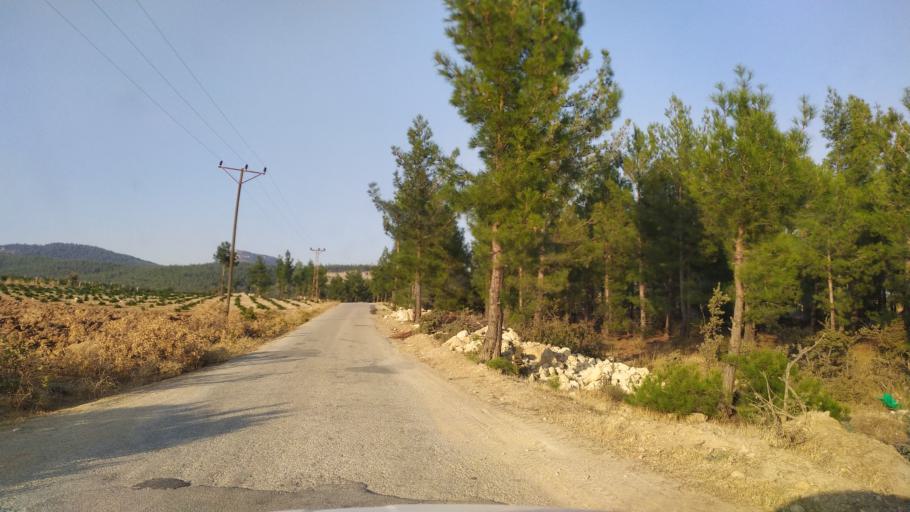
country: TR
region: Mersin
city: Mut
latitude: 36.6878
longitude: 33.1968
